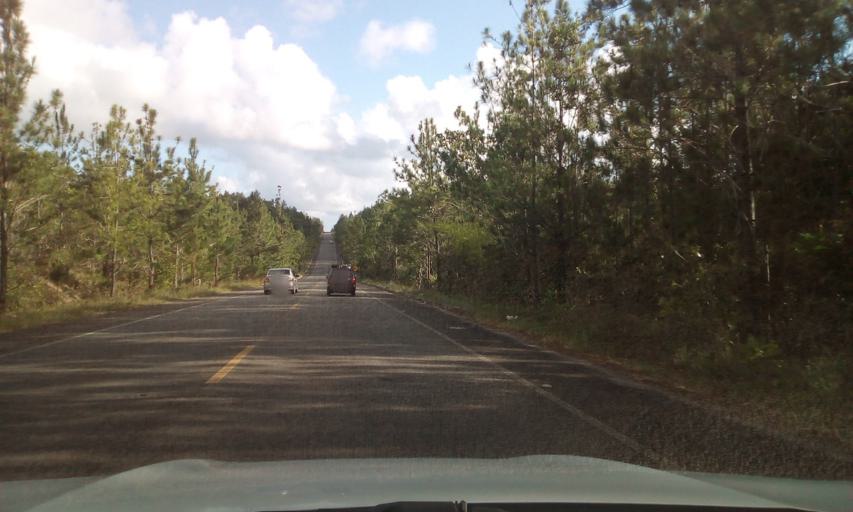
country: BR
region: Bahia
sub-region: Entre Rios
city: Entre Rios
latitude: -12.1284
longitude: -37.7912
